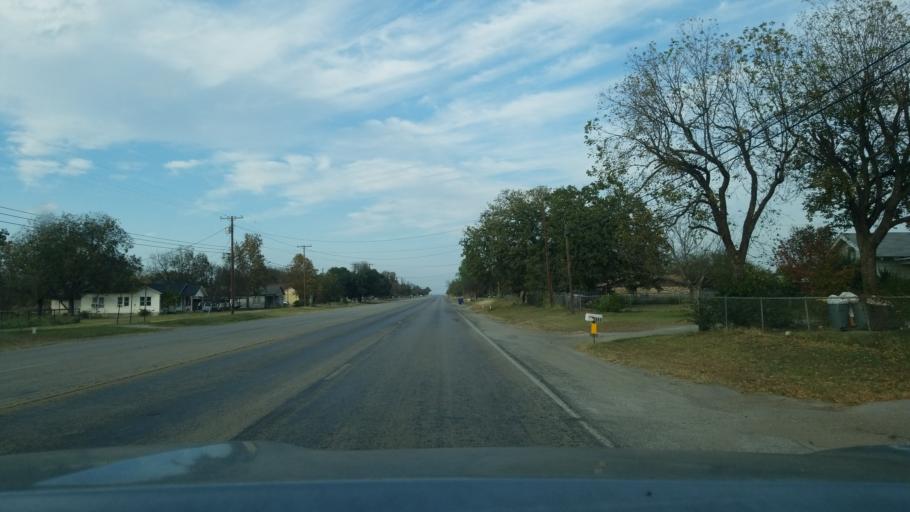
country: US
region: Texas
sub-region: Brown County
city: Early
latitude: 31.7626
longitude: -98.9567
